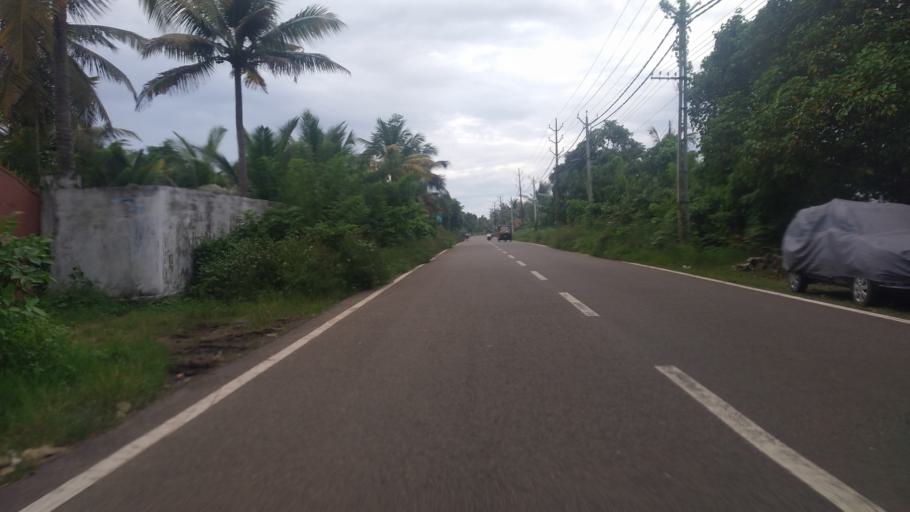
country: IN
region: Kerala
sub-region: Ernakulam
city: Cochin
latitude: 9.8603
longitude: 76.2688
